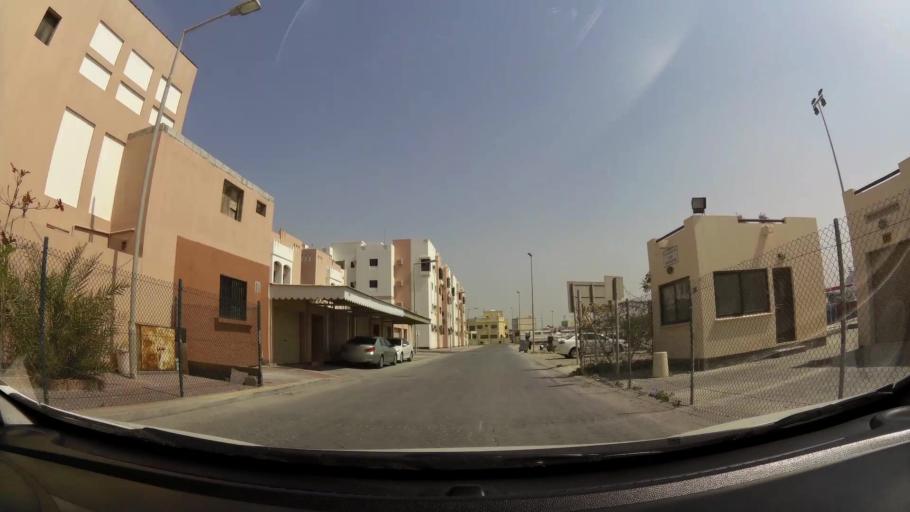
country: BH
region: Manama
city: Jidd Hafs
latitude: 26.2150
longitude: 50.4450
